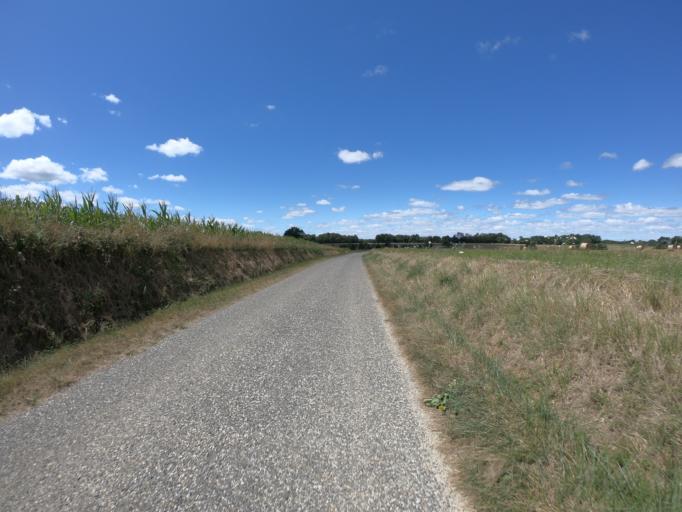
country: FR
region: Midi-Pyrenees
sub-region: Departement de l'Ariege
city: Verniolle
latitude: 43.0785
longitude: 1.7271
